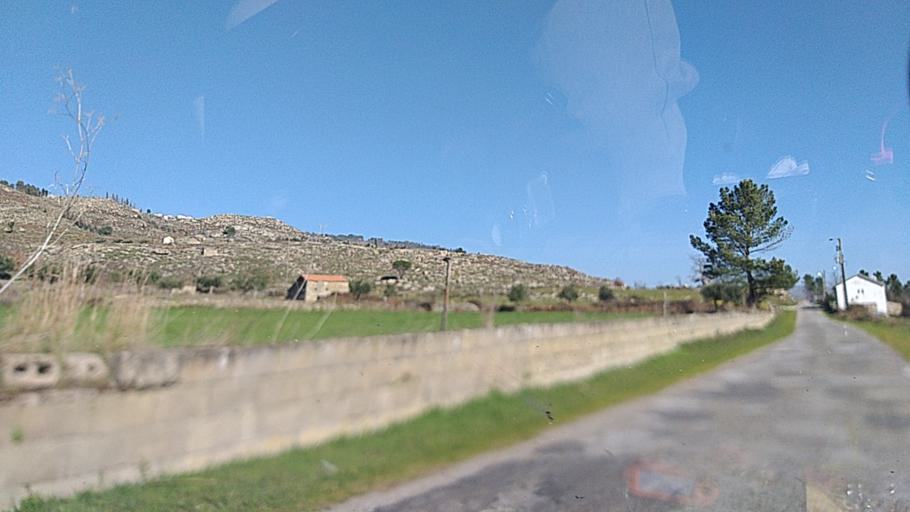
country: PT
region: Guarda
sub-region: Celorico da Beira
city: Celorico da Beira
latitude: 40.6673
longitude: -7.4585
